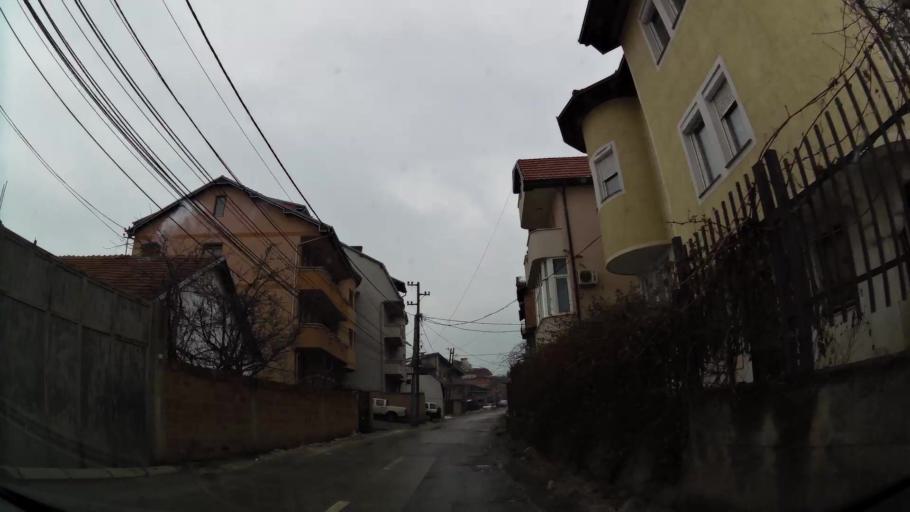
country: XK
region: Pristina
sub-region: Komuna e Prishtines
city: Pristina
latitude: 42.6818
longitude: 21.1785
